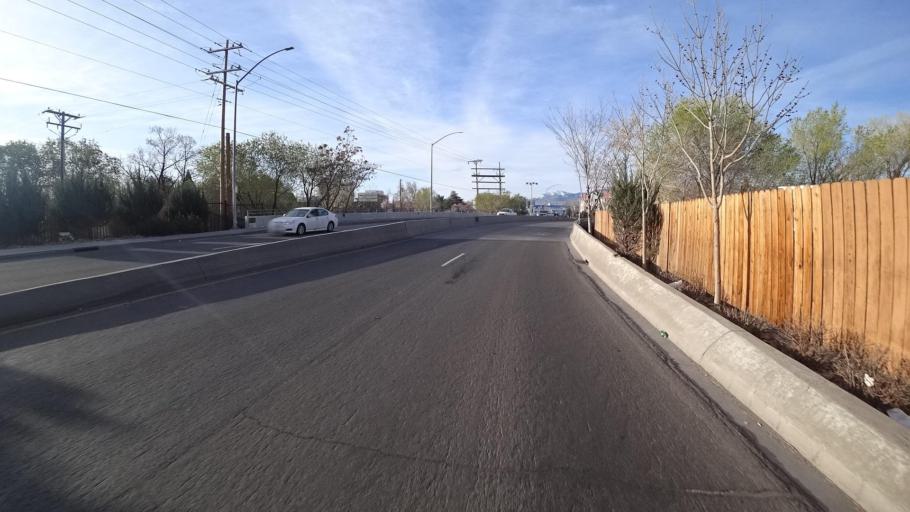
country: US
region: Nevada
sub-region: Washoe County
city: Reno
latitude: 39.5305
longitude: -119.7976
